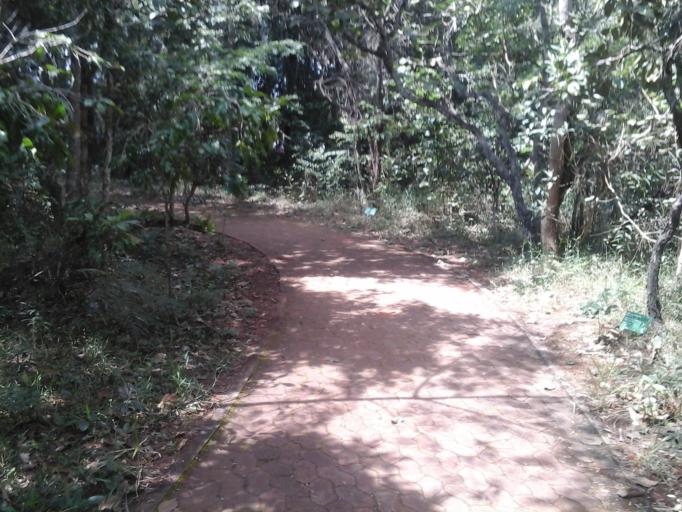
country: BR
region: Federal District
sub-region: Brasilia
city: Brasilia
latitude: -15.8737
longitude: -47.8358
